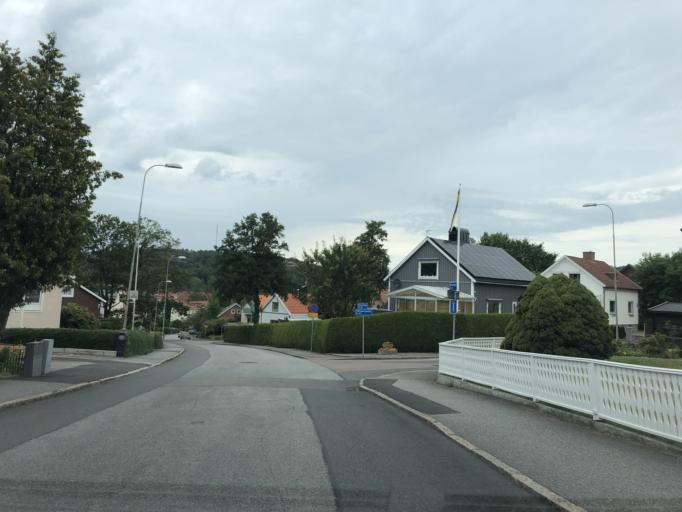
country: SE
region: Vaestra Goetaland
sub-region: Goteborg
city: Majorna
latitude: 57.7260
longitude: 11.9246
